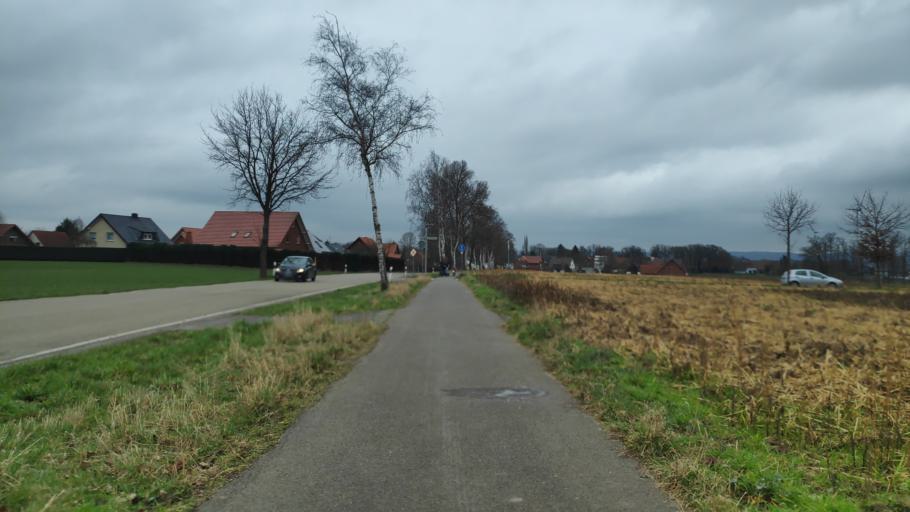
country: DE
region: North Rhine-Westphalia
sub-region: Regierungsbezirk Detmold
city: Hille
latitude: 52.3424
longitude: 8.7985
